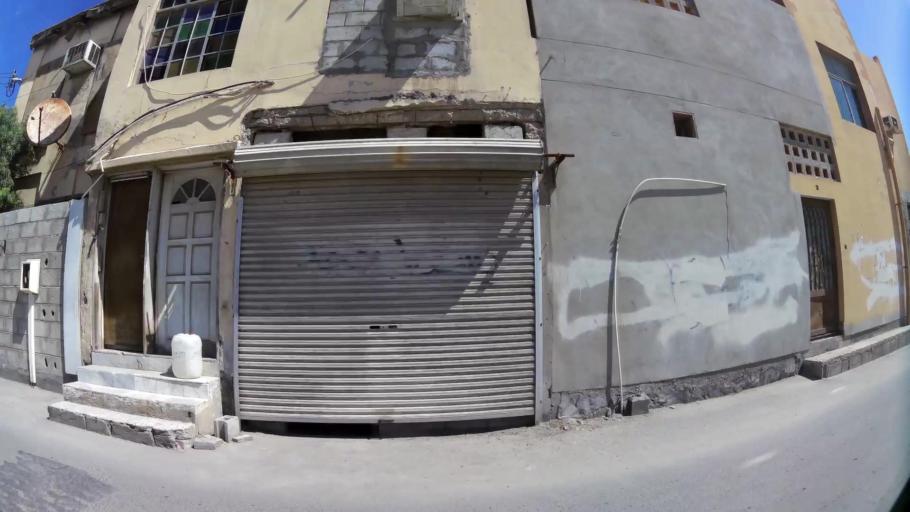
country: BH
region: Muharraq
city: Al Muharraq
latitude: 26.2789
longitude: 50.6340
